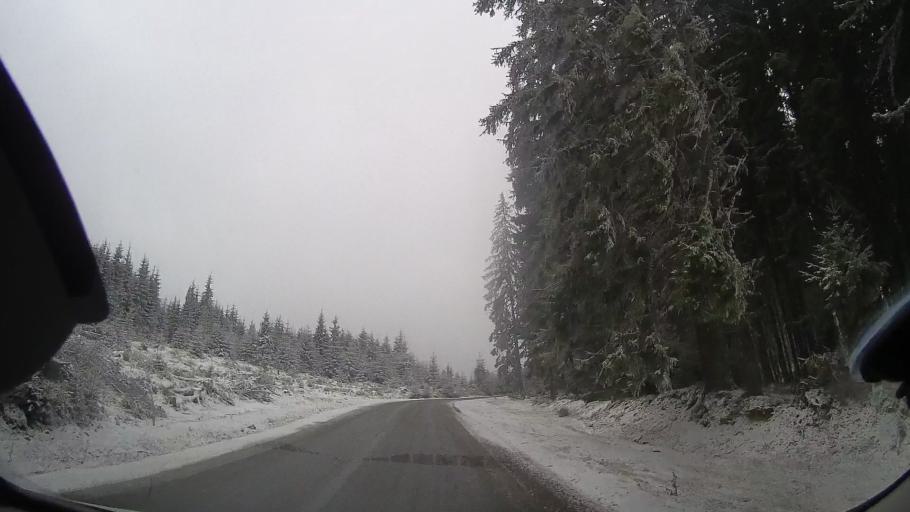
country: RO
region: Cluj
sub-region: Comuna Belis
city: Belis
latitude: 46.6406
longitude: 23.0573
